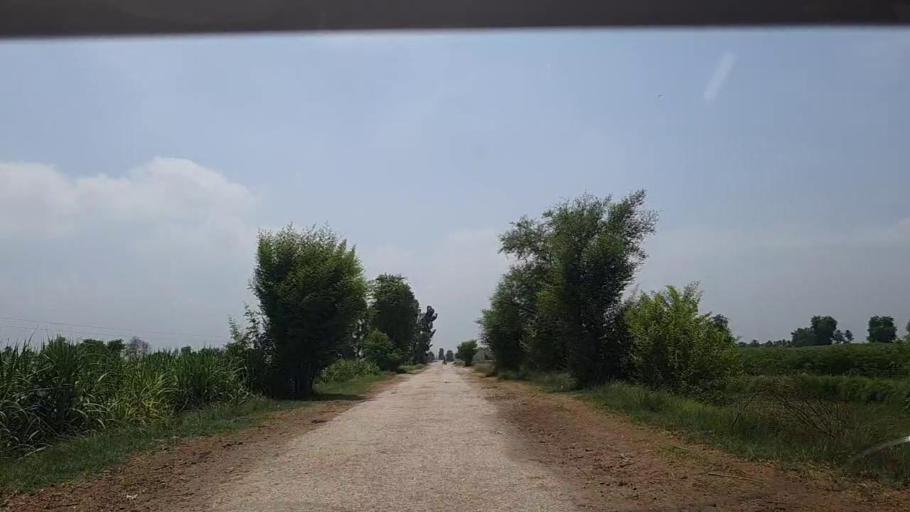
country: PK
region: Sindh
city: Khanpur
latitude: 27.9135
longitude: 69.3956
